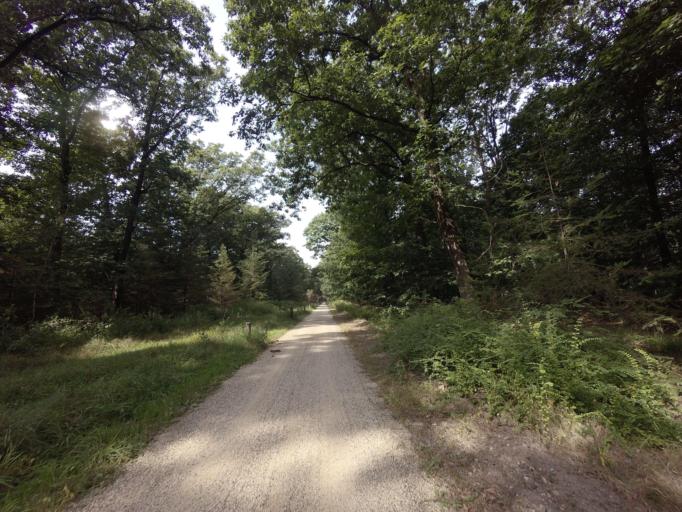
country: NL
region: North Brabant
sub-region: Gemeente Mill en Sint Hubert
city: Wilbertoord
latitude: 51.5377
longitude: 5.7879
